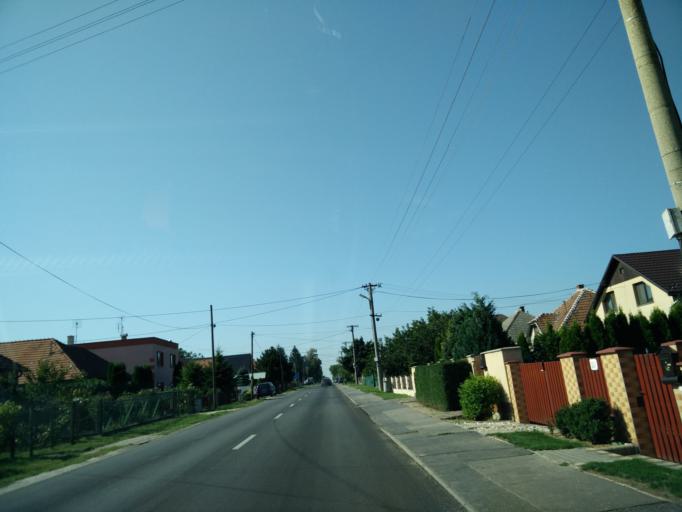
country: SK
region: Nitriansky
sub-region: Okres Nitra
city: Nitra
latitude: 48.4898
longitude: 18.1545
